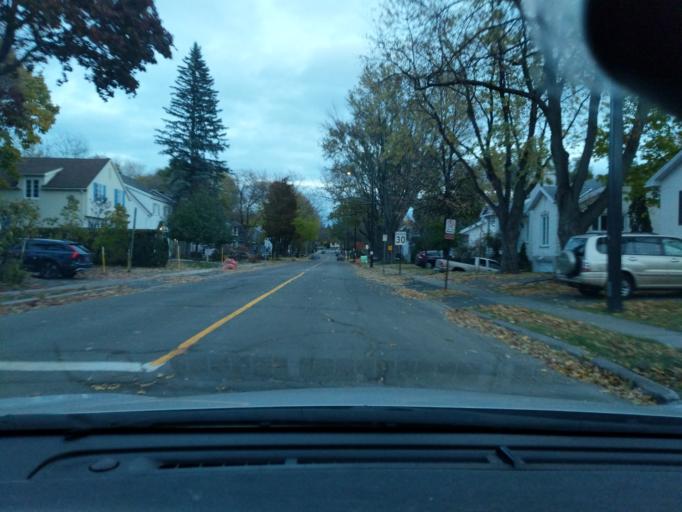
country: CA
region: Quebec
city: Quebec
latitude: 46.7902
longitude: -71.2515
